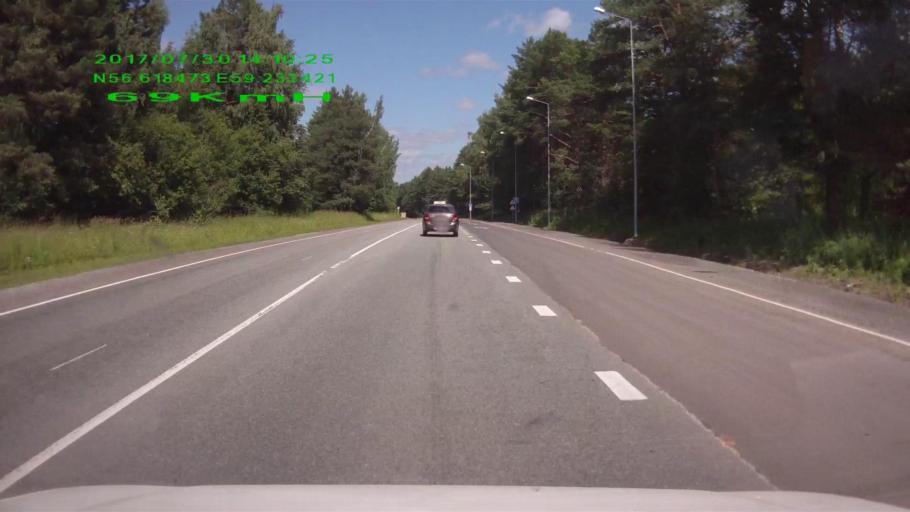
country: RU
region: Sverdlovsk
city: Nizhniye Sergi
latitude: 56.6187
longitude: 59.2337
